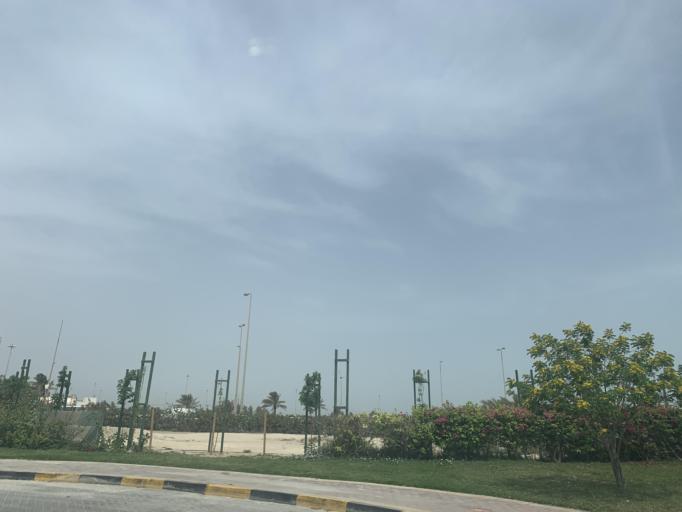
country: BH
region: Northern
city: Madinat `Isa
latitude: 26.1577
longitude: 50.5374
